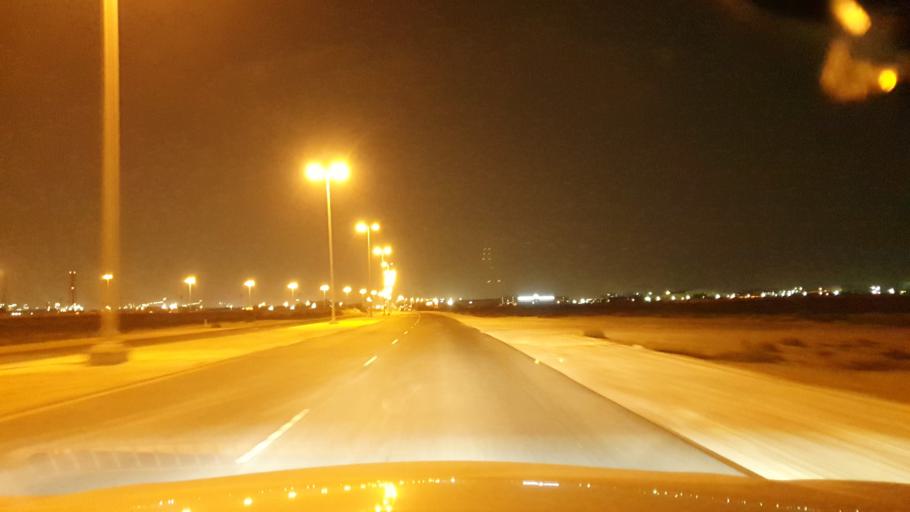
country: BH
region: Northern
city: Sitrah
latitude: 26.0664
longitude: 50.6168
